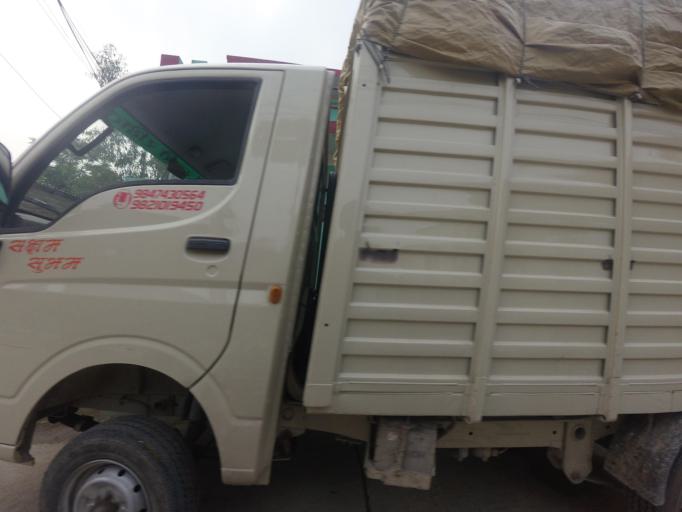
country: NP
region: Western Region
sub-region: Lumbini Zone
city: Bhairahawa
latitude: 27.5094
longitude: 83.4241
